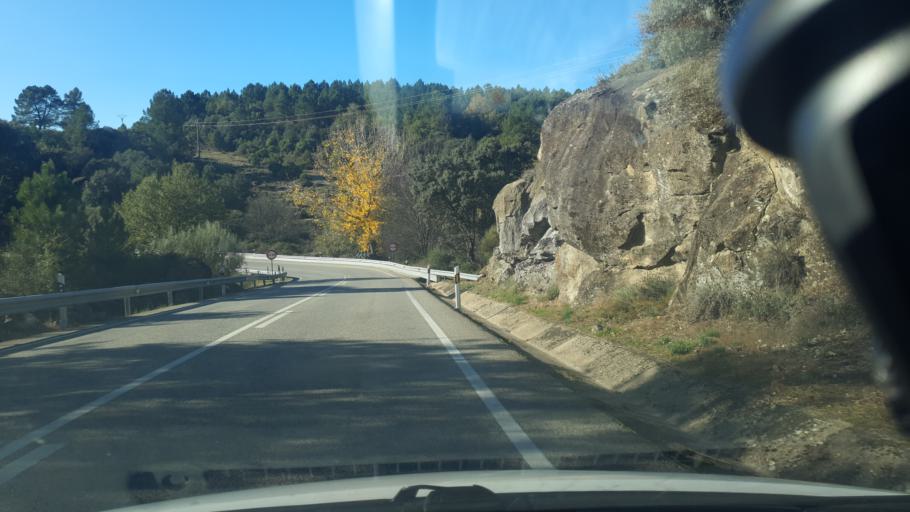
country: ES
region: Castille and Leon
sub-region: Provincia de Avila
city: Arenas de San Pedro
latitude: 40.1994
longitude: -5.0445
